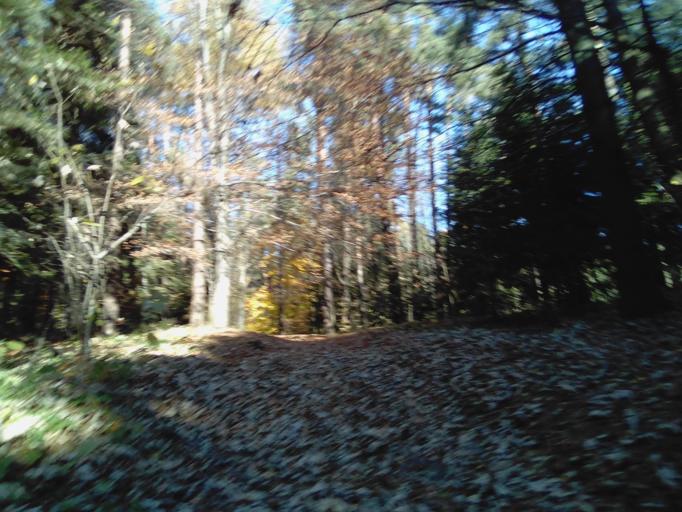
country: PL
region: Subcarpathian Voivodeship
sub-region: Powiat strzyzowski
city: Wysoka Strzyzowska
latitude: 49.8024
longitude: 21.7260
